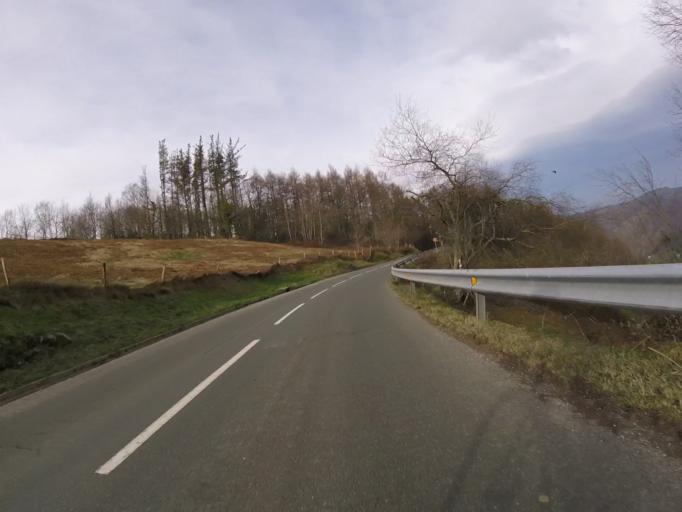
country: ES
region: Basque Country
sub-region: Provincia de Guipuzcoa
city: Beizama
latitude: 43.1533
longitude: -2.1975
